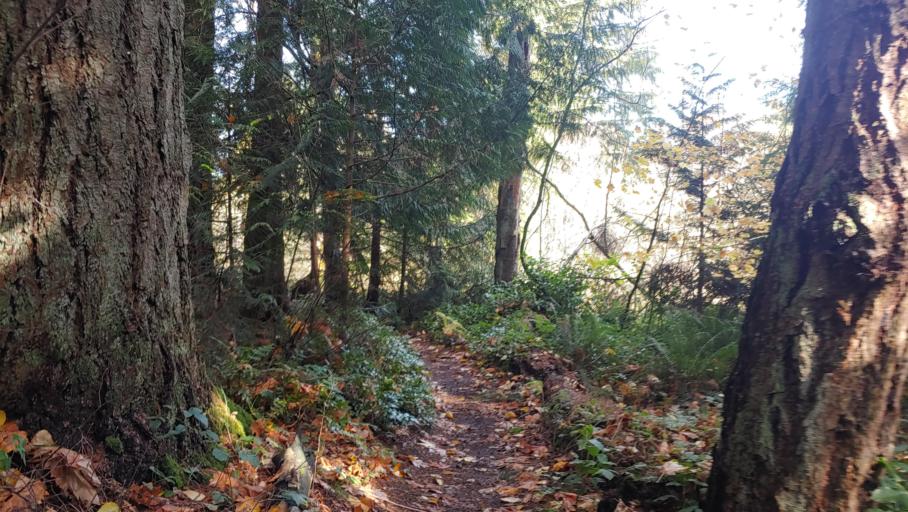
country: US
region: Washington
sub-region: King County
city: Fairwood
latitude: 47.4492
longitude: -122.1654
